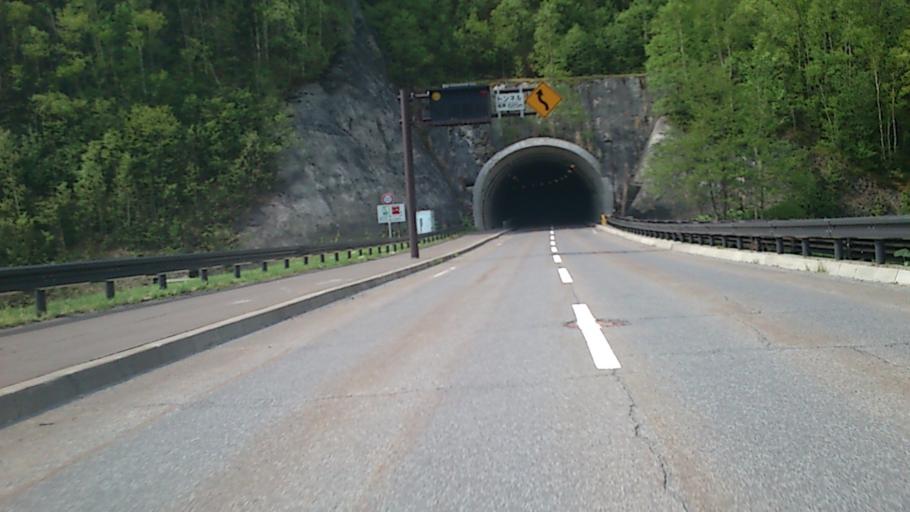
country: JP
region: Hokkaido
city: Kamikawa
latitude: 43.6753
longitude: 143.0359
